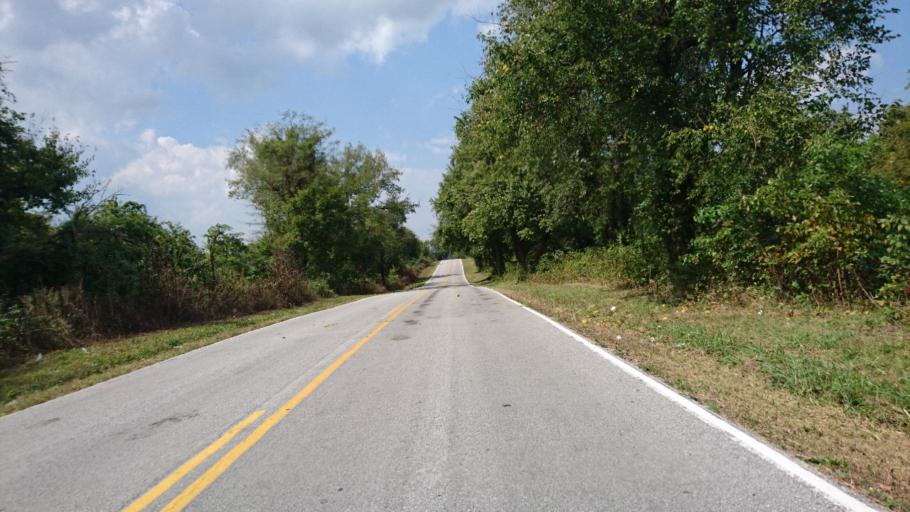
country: US
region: Missouri
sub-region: Greene County
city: Springfield
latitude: 37.1979
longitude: -93.3787
